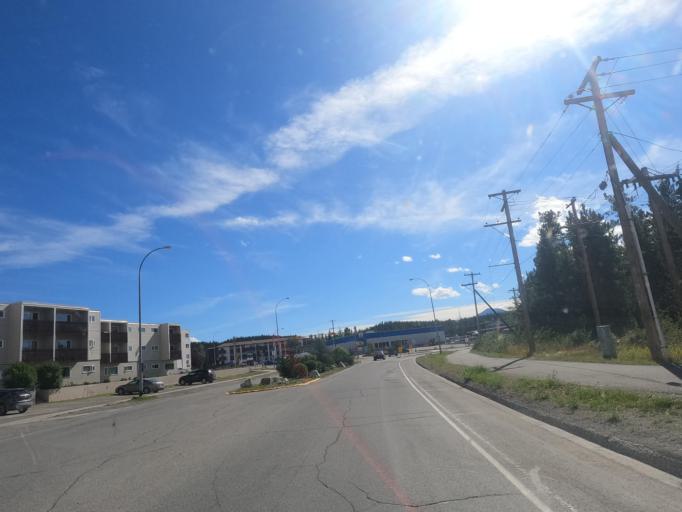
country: CA
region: Yukon
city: Whitehorse
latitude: 60.7069
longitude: -135.0346
